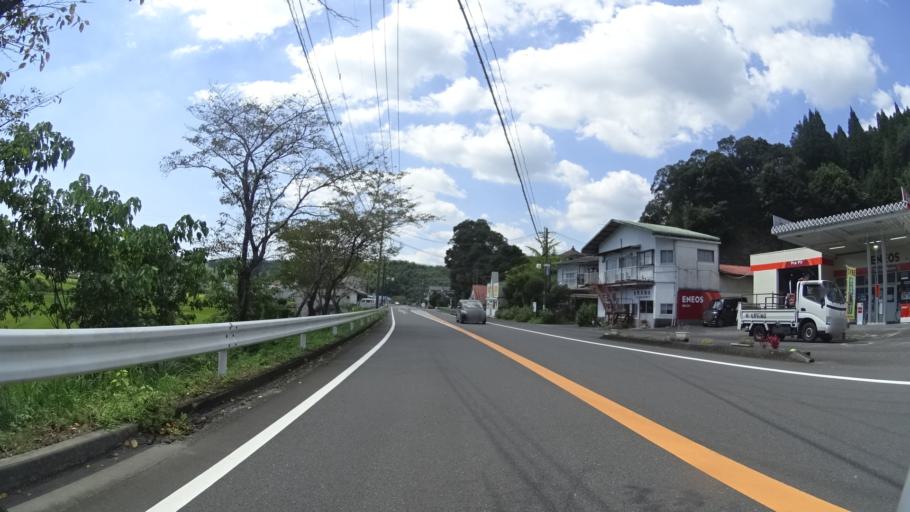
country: JP
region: Kagoshima
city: Kokubu-matsuki
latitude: 31.8590
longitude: 130.7586
